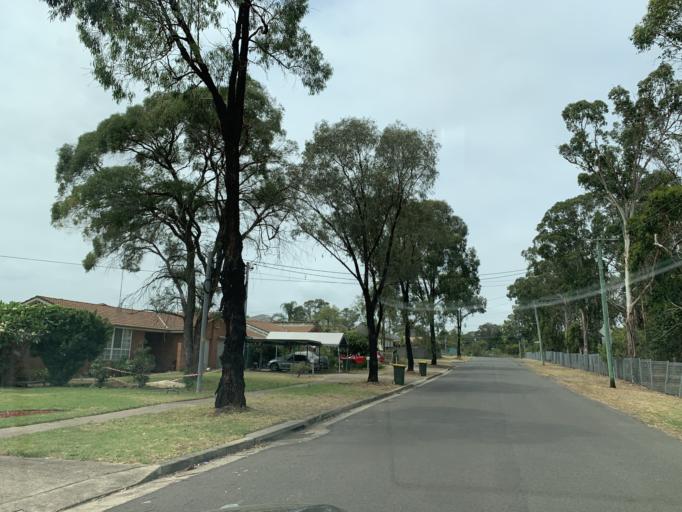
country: AU
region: New South Wales
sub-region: Blacktown
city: Doonside
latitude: -33.7627
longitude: 150.8855
